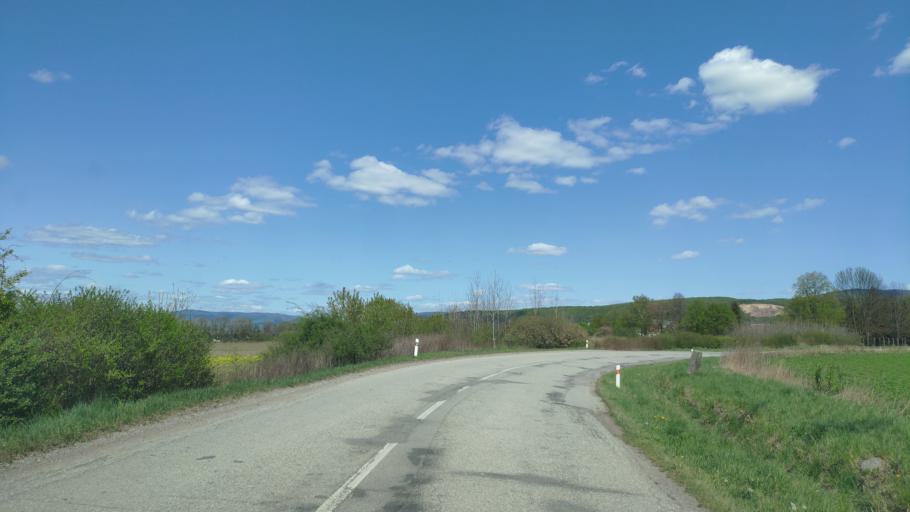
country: SK
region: Kosicky
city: Kosice
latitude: 48.6797
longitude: 21.4228
